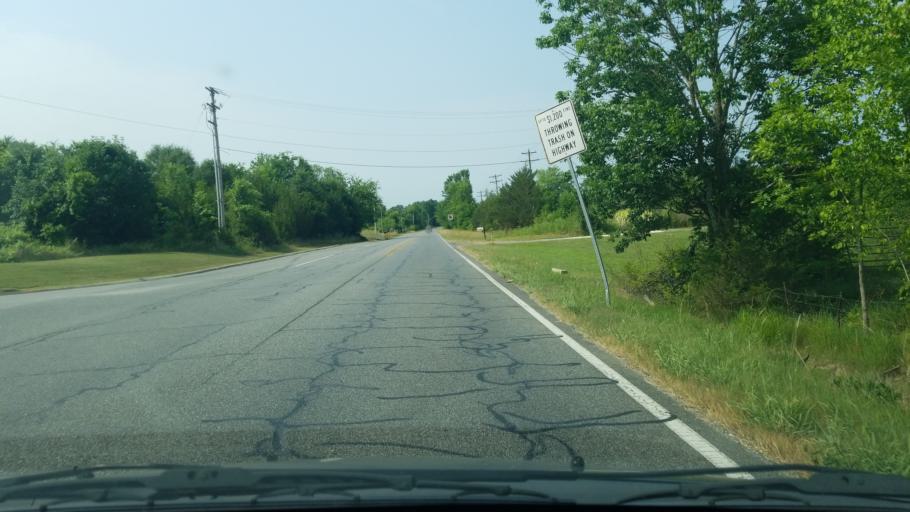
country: US
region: Tennessee
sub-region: Hamilton County
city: East Brainerd
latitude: 34.9824
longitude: -85.0969
